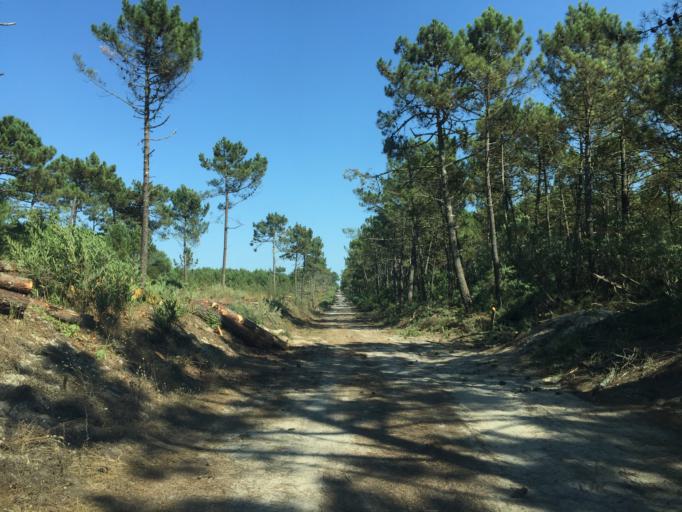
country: PT
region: Coimbra
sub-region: Figueira da Foz
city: Tavarede
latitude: 40.2627
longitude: -8.8605
